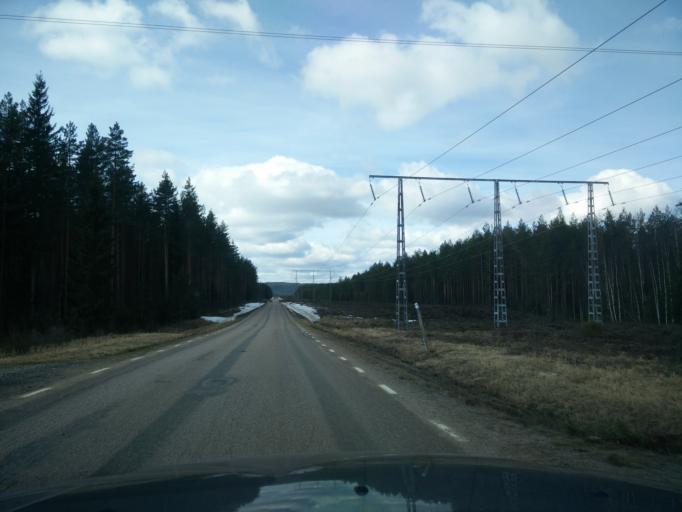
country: SE
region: Vaermland
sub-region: Hagfors Kommun
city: Hagfors
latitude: 60.0358
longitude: 13.5566
